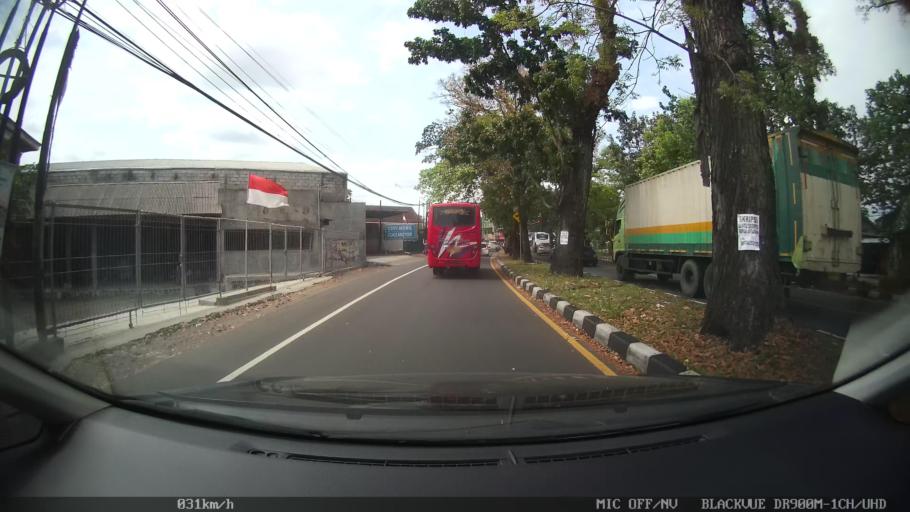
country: ID
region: Central Java
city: Candi Prambanan
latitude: -7.7580
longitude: 110.4794
